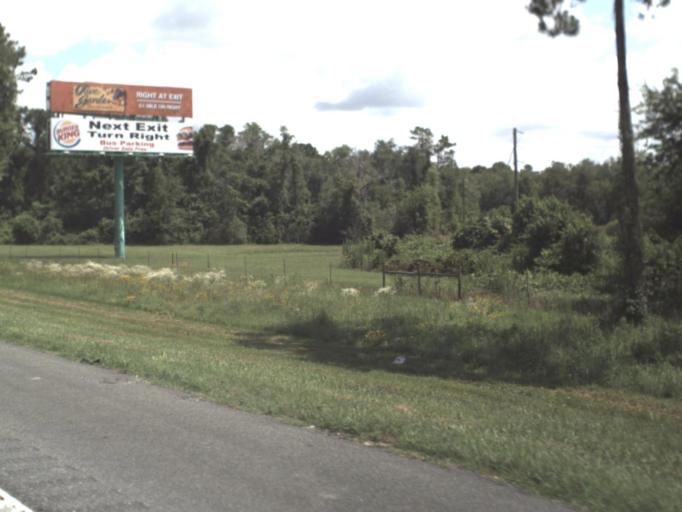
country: US
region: Florida
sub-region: Columbia County
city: Lake City
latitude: 30.1299
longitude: -82.6627
